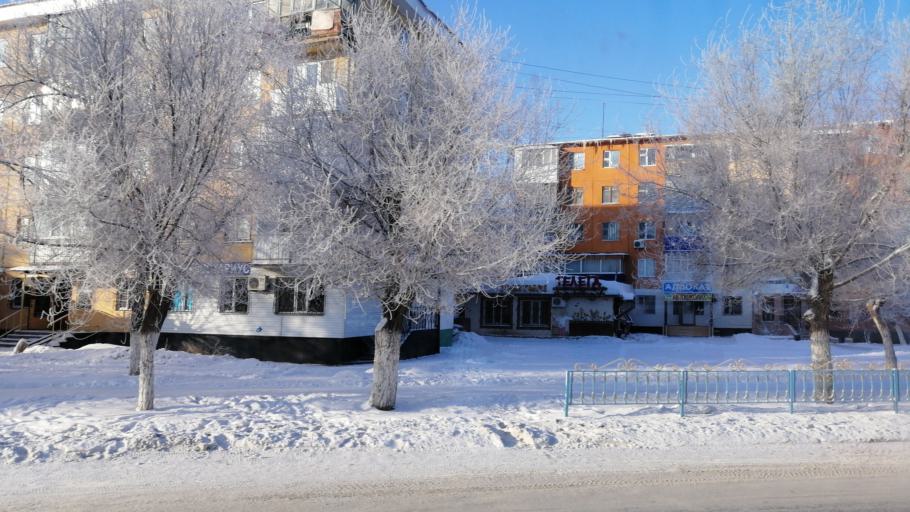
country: KZ
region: Aqtoebe
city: Aqtobe
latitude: 50.3078
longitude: 57.1491
